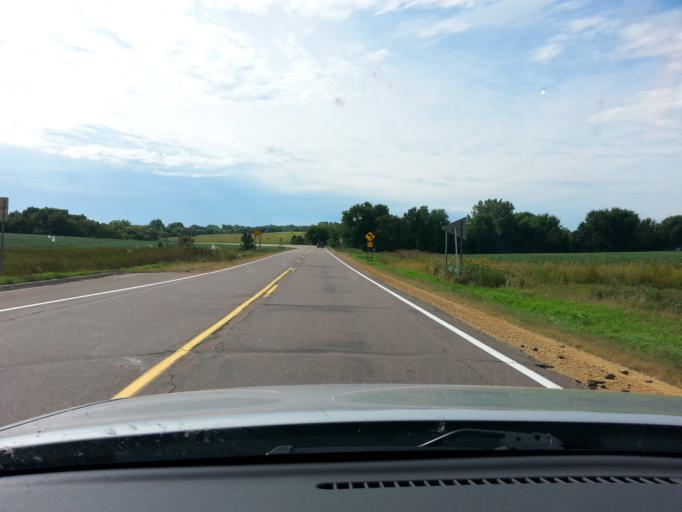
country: US
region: Minnesota
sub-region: Goodhue County
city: Cannon Falls
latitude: 44.6042
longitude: -92.9999
